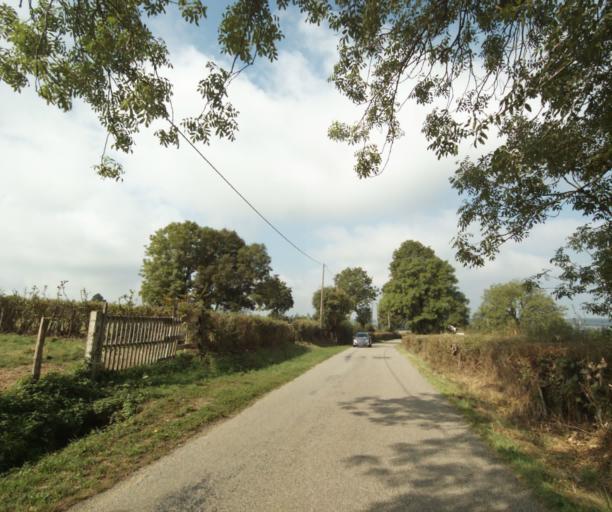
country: FR
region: Bourgogne
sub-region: Departement de Saone-et-Loire
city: Charolles
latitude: 46.4273
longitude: 4.2917
